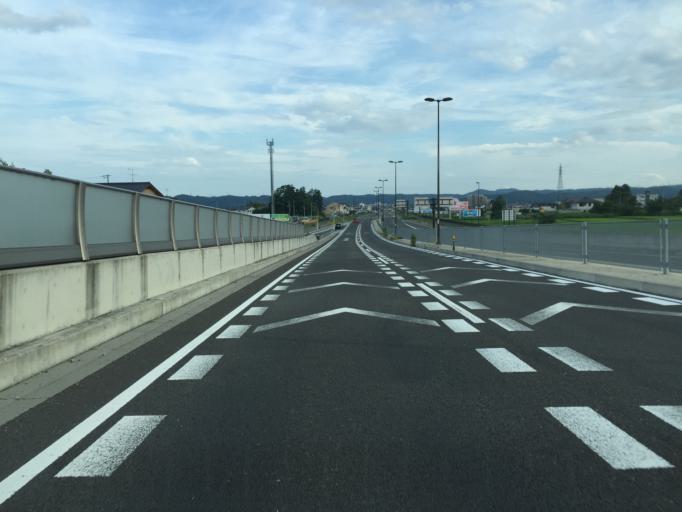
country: JP
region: Fukushima
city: Fukushima-shi
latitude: 37.7391
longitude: 140.4402
